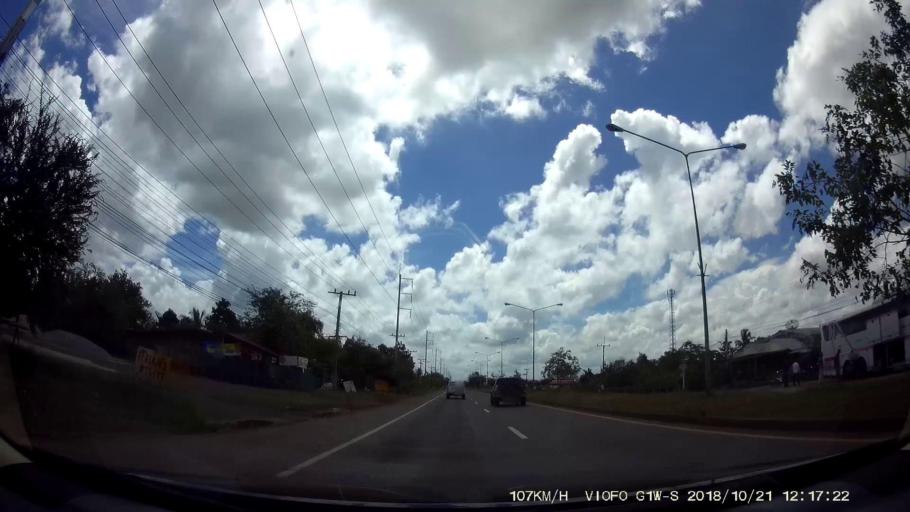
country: TH
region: Nakhon Ratchasima
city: Dan Khun Thot
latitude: 15.3331
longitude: 101.8208
